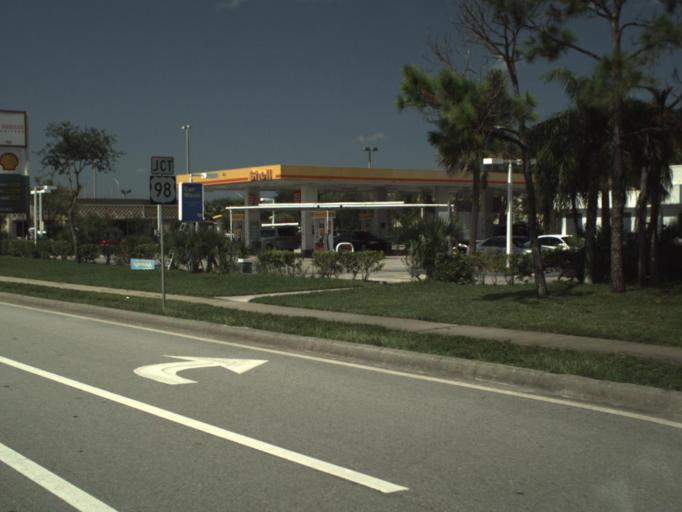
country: US
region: Florida
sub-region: Palm Beach County
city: Royal Palm Beach
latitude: 26.6772
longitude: -80.2023
